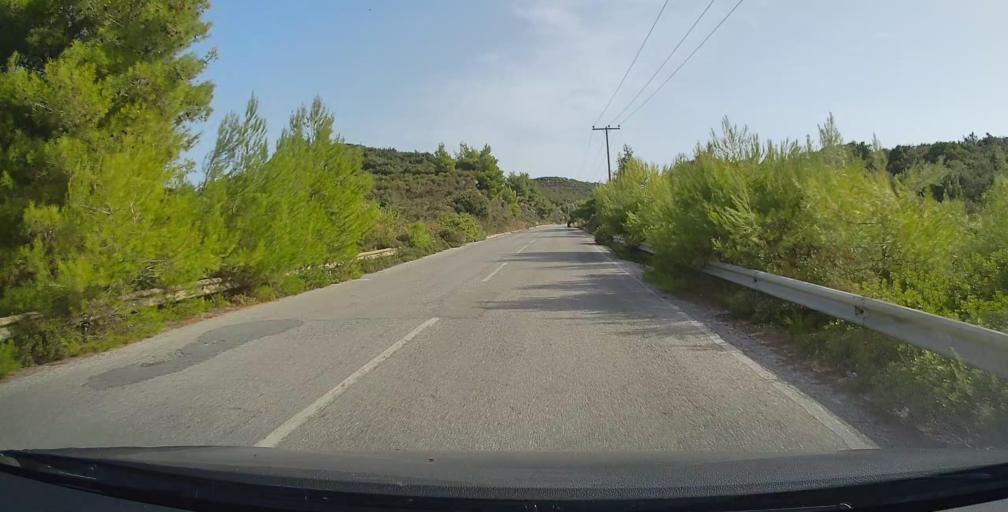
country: GR
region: Central Macedonia
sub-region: Nomos Chalkidikis
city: Sykia
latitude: 39.9662
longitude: 23.9498
